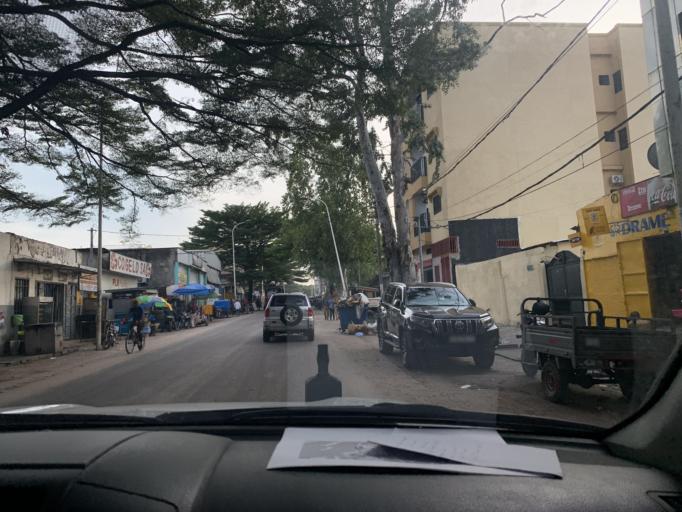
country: CG
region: Brazzaville
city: Brazzaville
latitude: -4.2640
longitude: 15.2881
